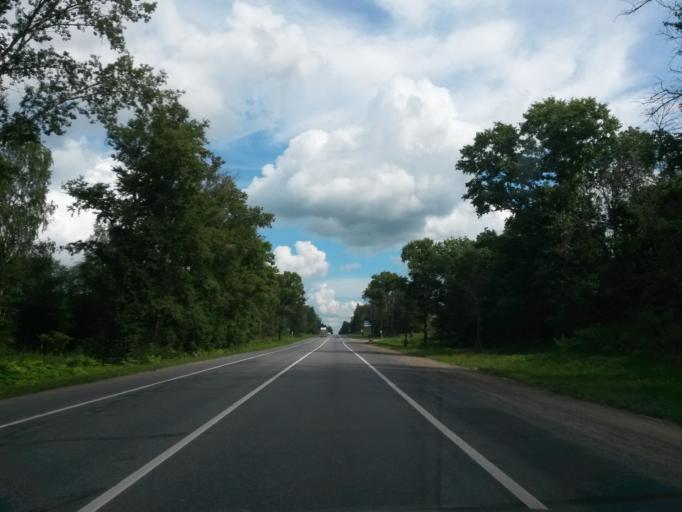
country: RU
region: Jaroslavl
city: Pereslavl'-Zalesskiy
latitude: 56.6649
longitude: 38.7143
